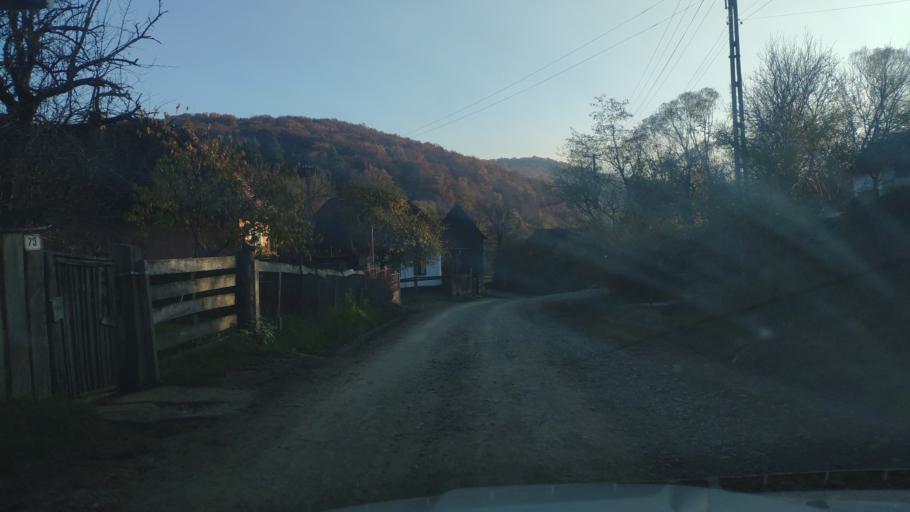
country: RO
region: Mures
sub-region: Comuna Ghindari
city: Ghindari
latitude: 46.5231
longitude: 24.9153
